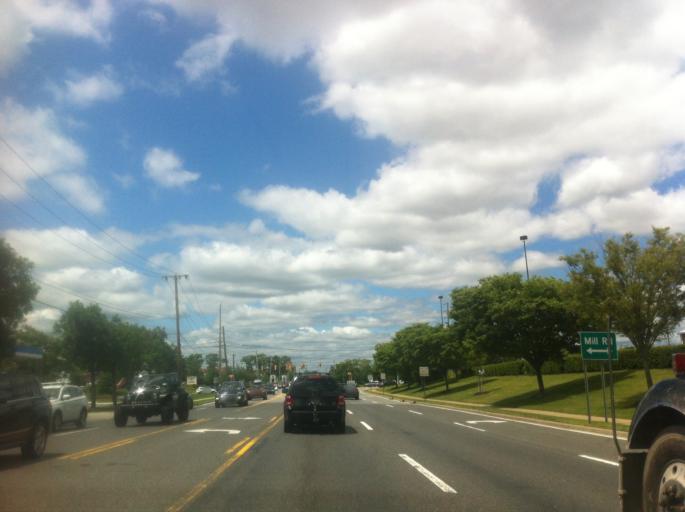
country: US
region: New York
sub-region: Suffolk County
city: Riverhead
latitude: 40.9257
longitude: -72.6944
